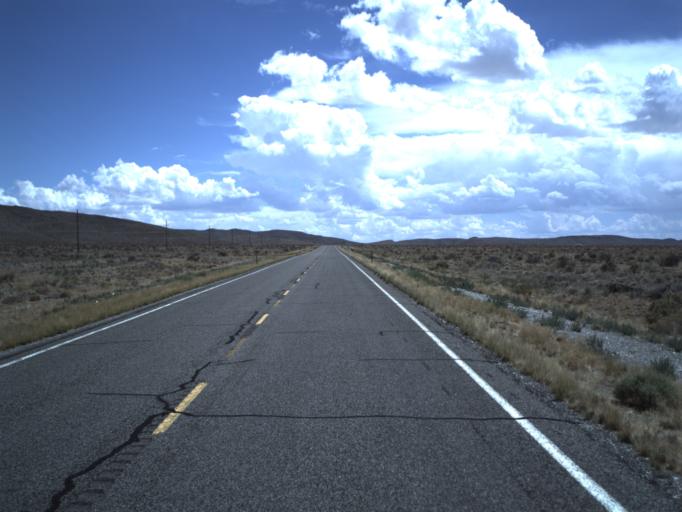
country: US
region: Utah
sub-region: Beaver County
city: Milford
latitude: 39.0319
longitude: -113.3845
